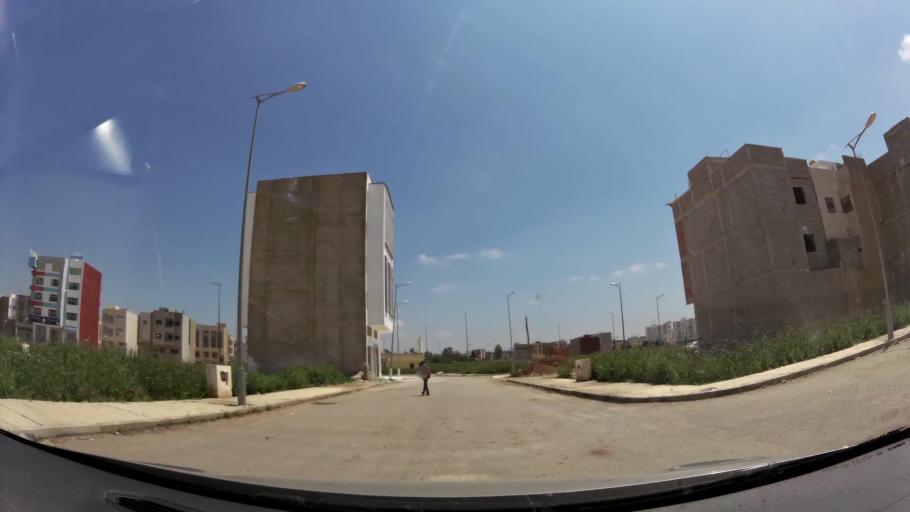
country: MA
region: Fes-Boulemane
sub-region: Fes
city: Fes
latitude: 34.0224
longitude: -5.0600
